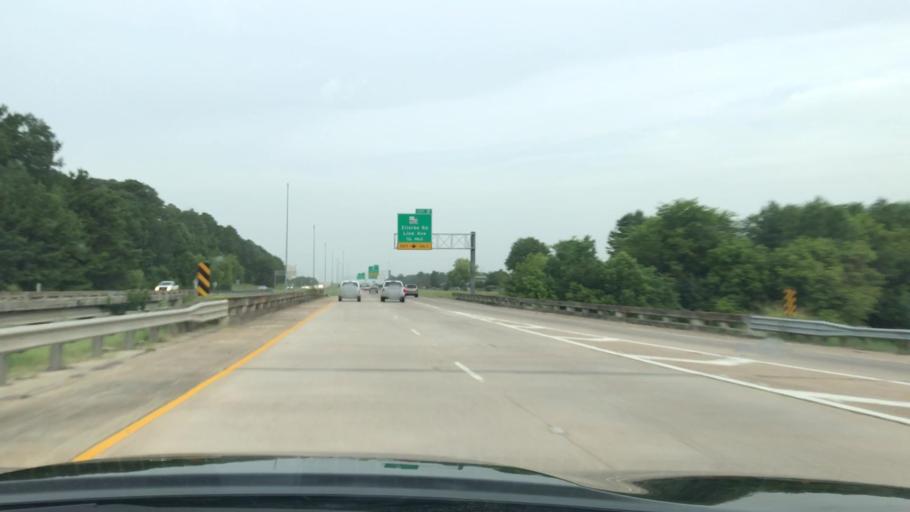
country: US
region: Louisiana
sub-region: Bossier Parish
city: Bossier City
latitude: 32.4127
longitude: -93.7278
